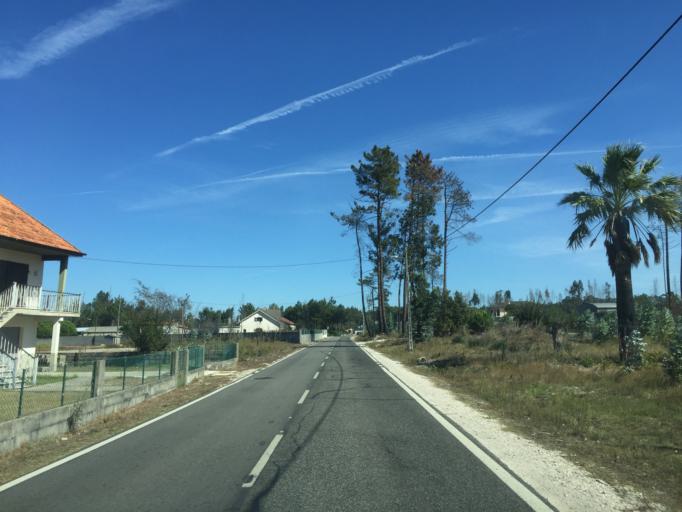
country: PT
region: Coimbra
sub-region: Figueira da Foz
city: Alhadas
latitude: 40.2212
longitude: -8.8259
